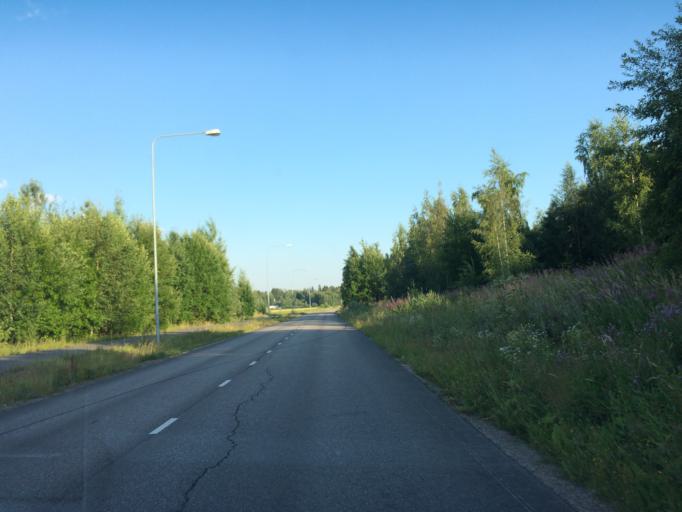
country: FI
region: Haeme
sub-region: Haemeenlinna
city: Parola
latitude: 61.0429
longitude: 24.3790
